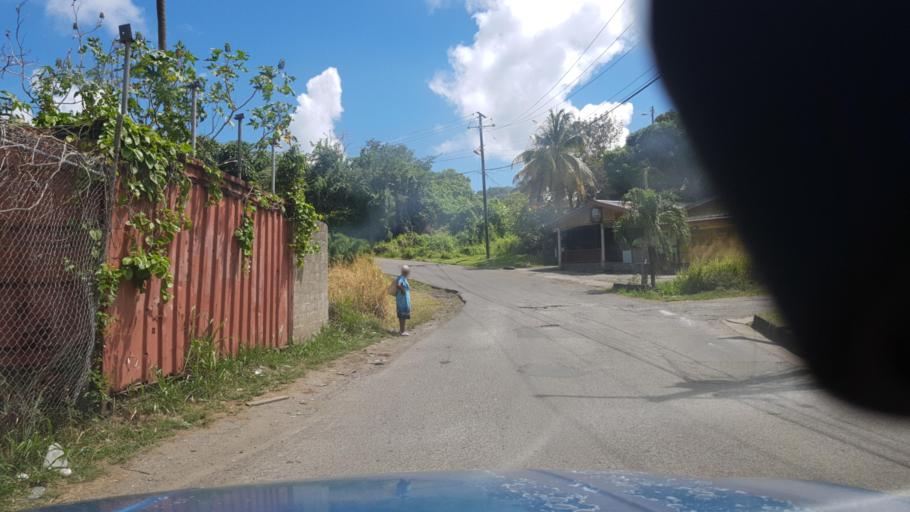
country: LC
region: Gros-Islet
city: Gros Islet
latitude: 14.0605
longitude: -60.9444
